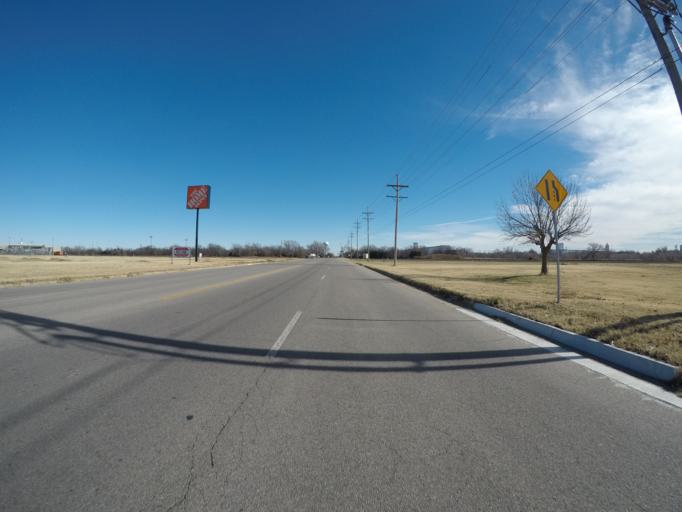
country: US
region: Kansas
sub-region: Reno County
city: Hutchinson
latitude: 38.0649
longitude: -97.8952
